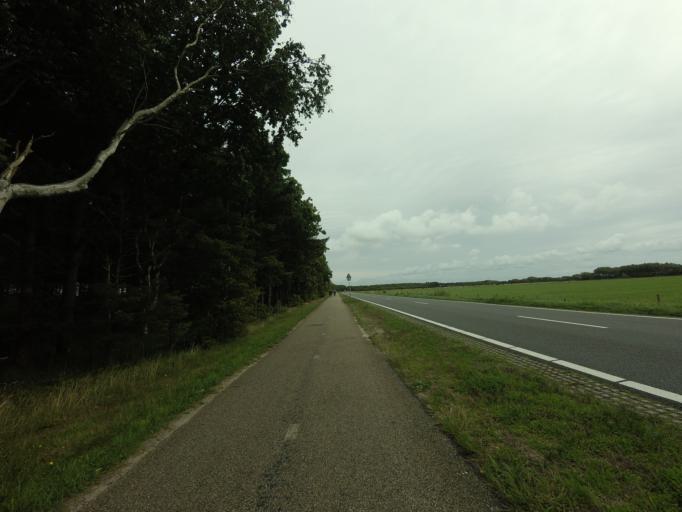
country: NL
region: Friesland
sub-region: Gemeente Ameland
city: Hollum
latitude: 53.4465
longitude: 5.7025
